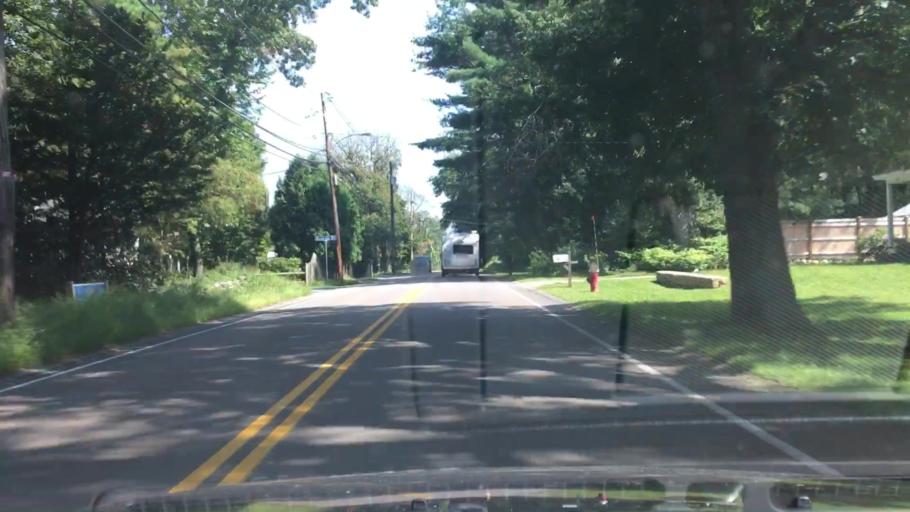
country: US
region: Massachusetts
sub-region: Middlesex County
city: Holliston
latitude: 42.2008
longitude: -71.4129
